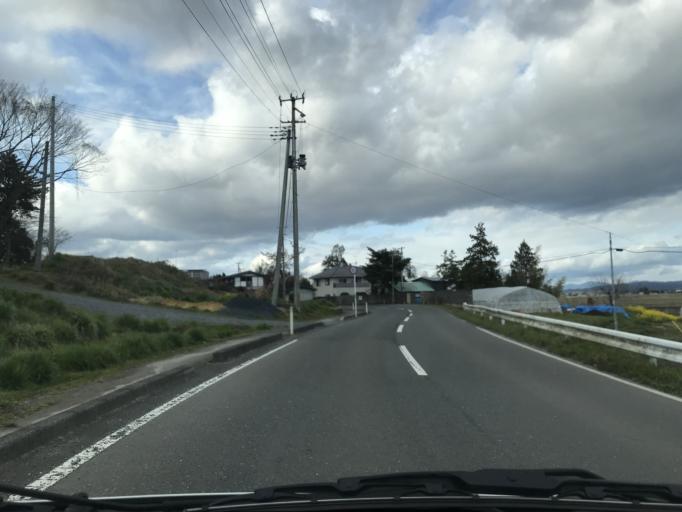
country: JP
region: Miyagi
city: Wakuya
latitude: 38.6445
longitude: 141.2163
